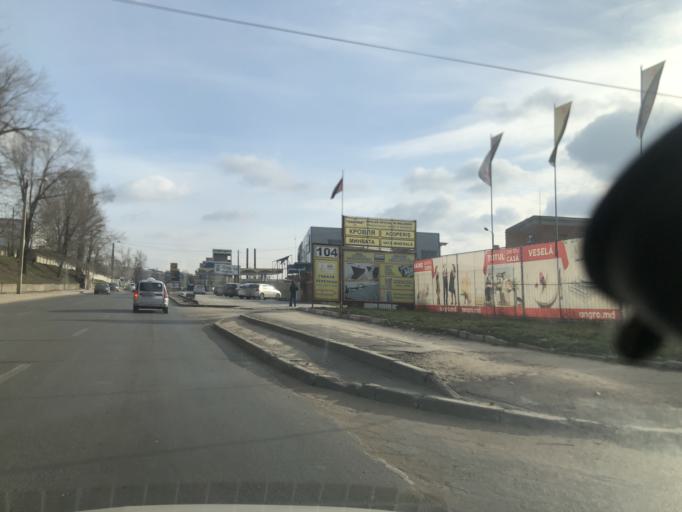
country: MD
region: Chisinau
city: Chisinau
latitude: 46.9962
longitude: 28.9010
